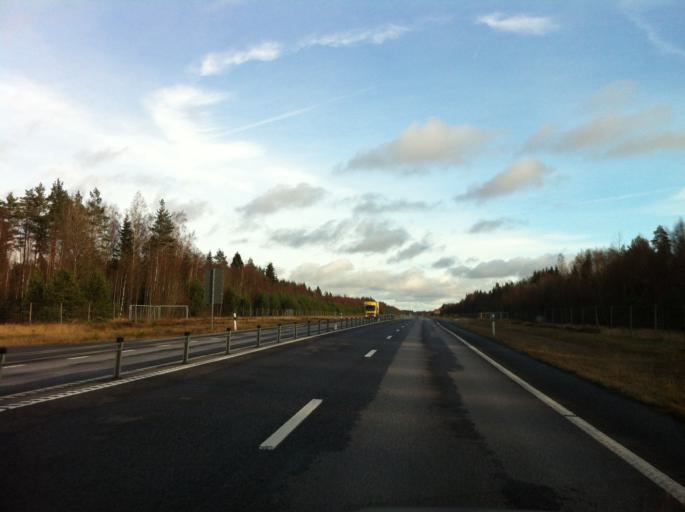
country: SE
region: Kronoberg
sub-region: Alvesta Kommun
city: Vislanda
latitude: 56.6659
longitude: 14.3050
